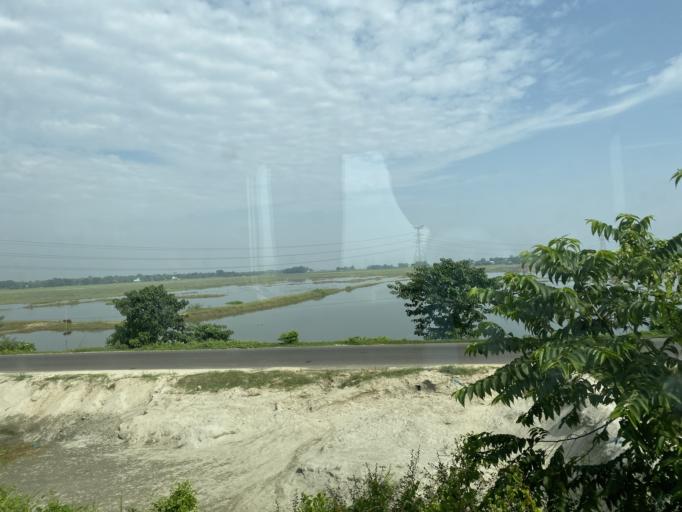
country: IN
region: Tripura
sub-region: West Tripura
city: Agartala
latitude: 23.8797
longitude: 91.1973
